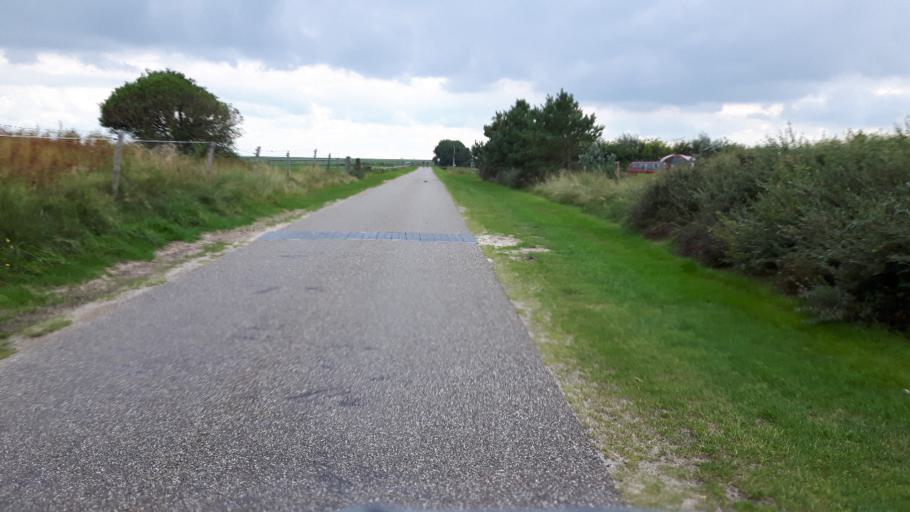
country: NL
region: Friesland
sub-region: Gemeente Ameland
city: Nes
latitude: 53.4516
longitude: 5.8177
